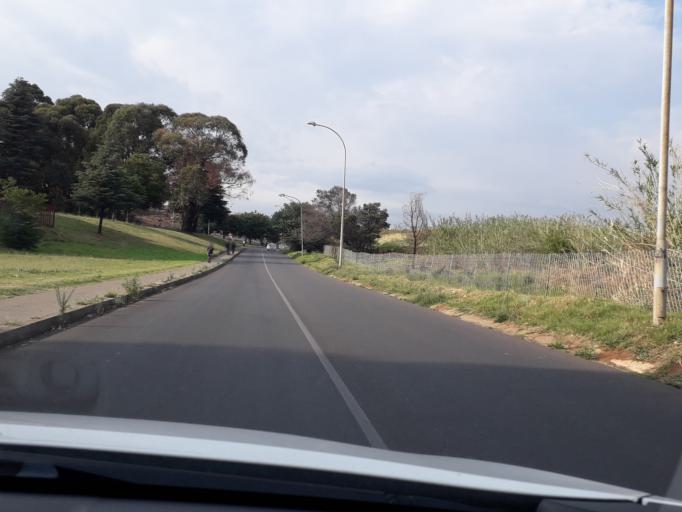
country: ZA
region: Gauteng
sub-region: City of Johannesburg Metropolitan Municipality
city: Johannesburg
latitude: -26.1678
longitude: 27.9753
